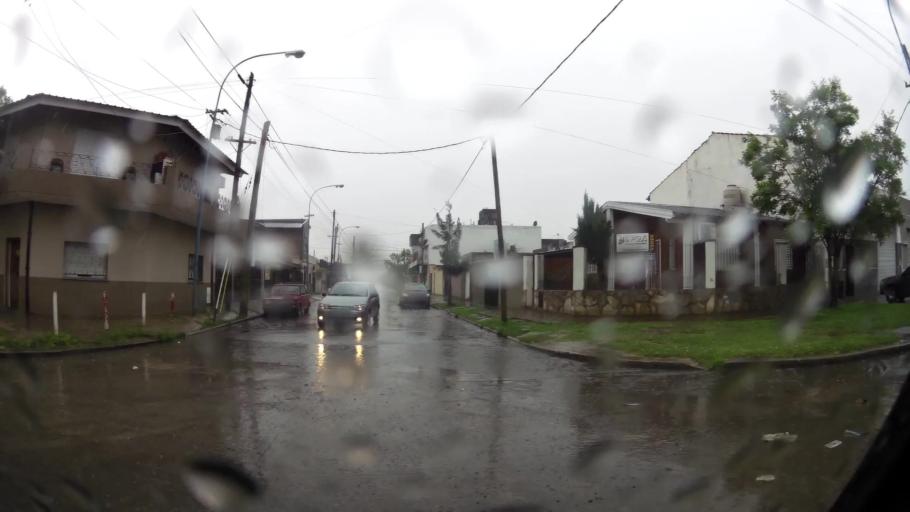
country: AR
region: Buenos Aires
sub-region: Partido de Lanus
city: Lanus
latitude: -34.7183
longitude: -58.4073
